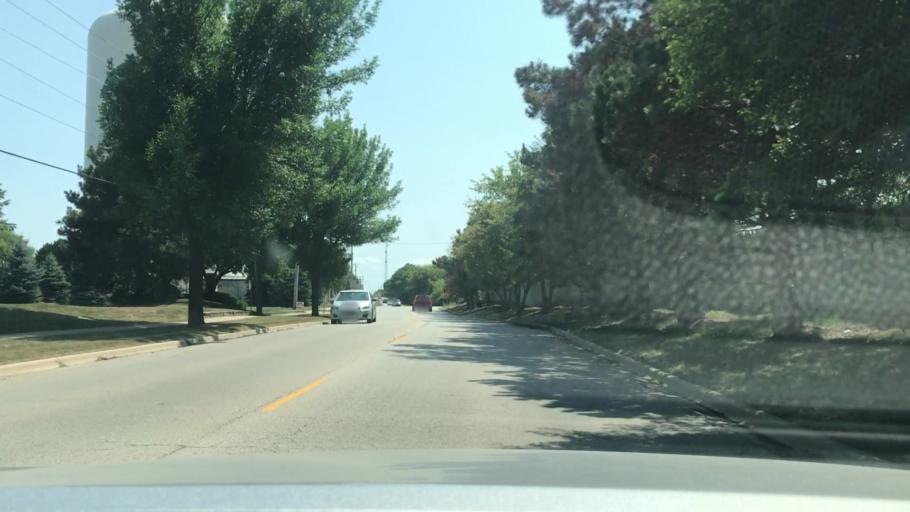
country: US
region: Illinois
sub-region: Kane County
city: Aurora
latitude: 41.7264
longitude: -88.2353
